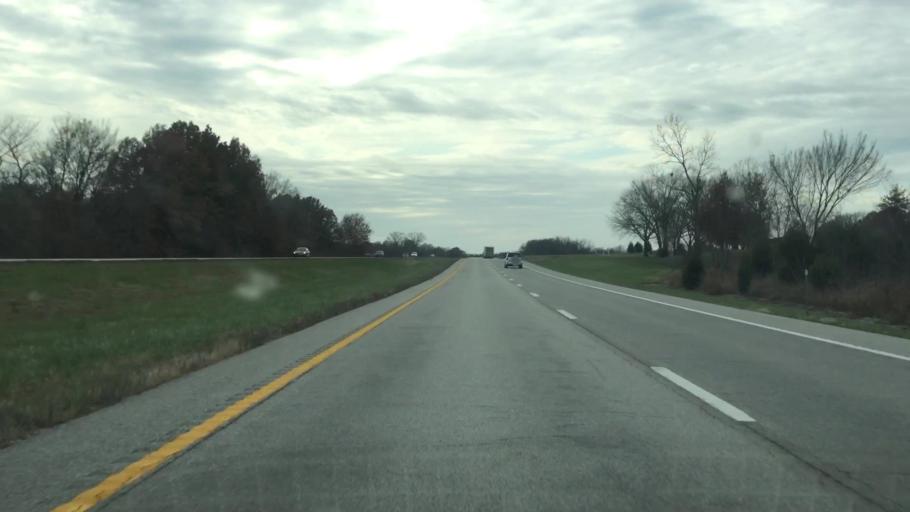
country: US
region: Missouri
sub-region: Cass County
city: Garden City
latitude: 38.5175
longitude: -94.1231
